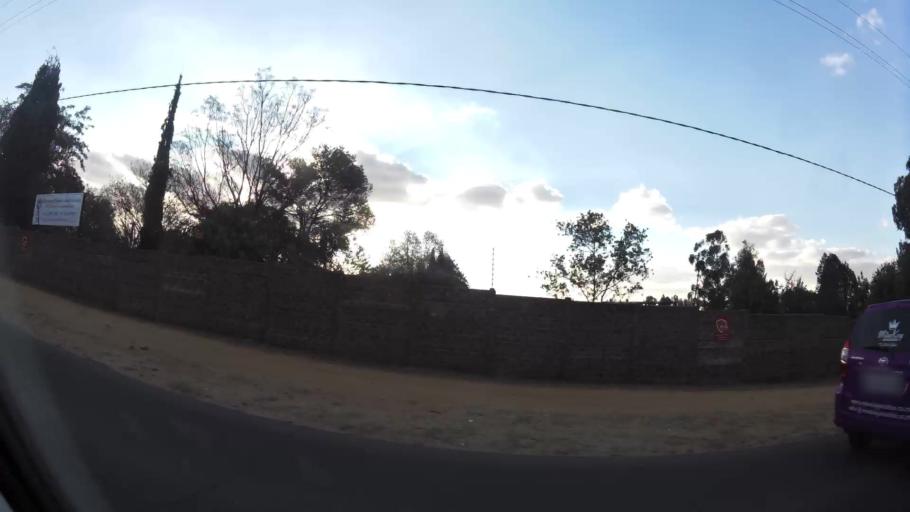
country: ZA
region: Gauteng
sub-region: City of Johannesburg Metropolitan Municipality
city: Diepsloot
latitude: -26.0004
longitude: 28.0016
